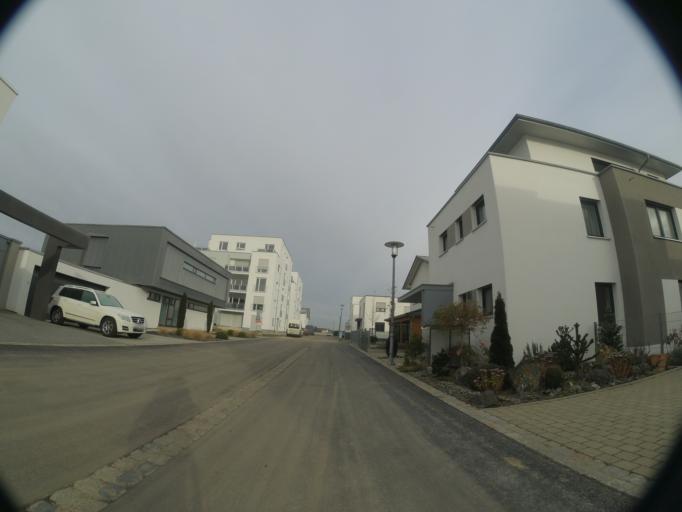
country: DE
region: Bavaria
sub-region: Swabia
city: Neu-Ulm
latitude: 48.4354
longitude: 10.0187
